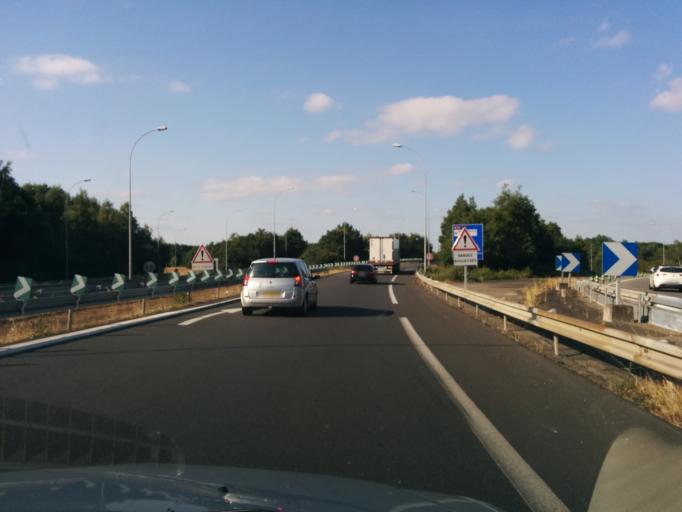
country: FR
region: Pays de la Loire
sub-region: Departement de la Loire-Atlantique
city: Carquefou
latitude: 47.2879
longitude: -1.4790
